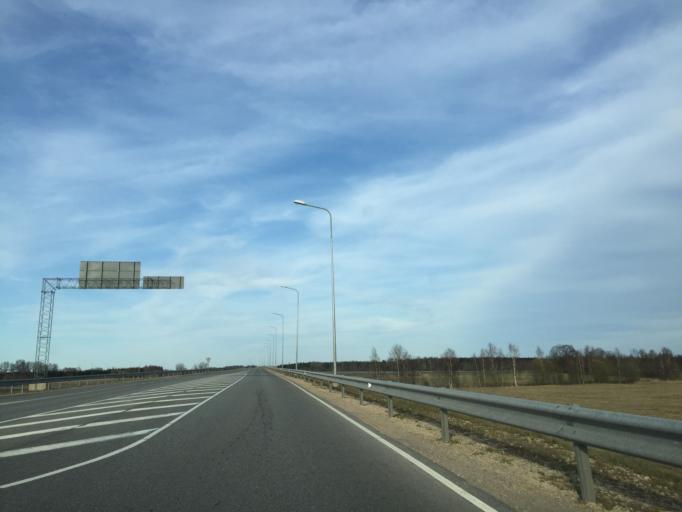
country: LV
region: Lielvarde
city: Lielvarde
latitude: 56.8050
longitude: 24.8763
